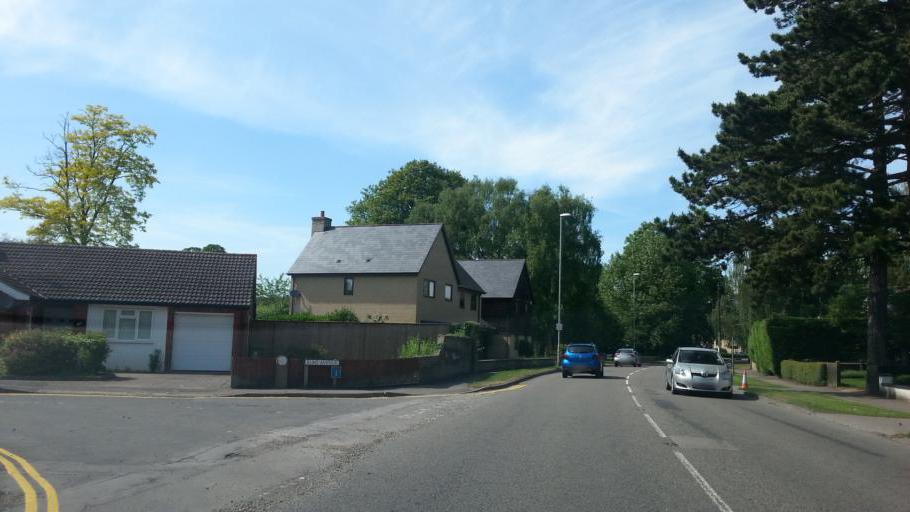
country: GB
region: England
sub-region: Cambridgeshire
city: Sawston
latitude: 52.1487
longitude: 0.1367
